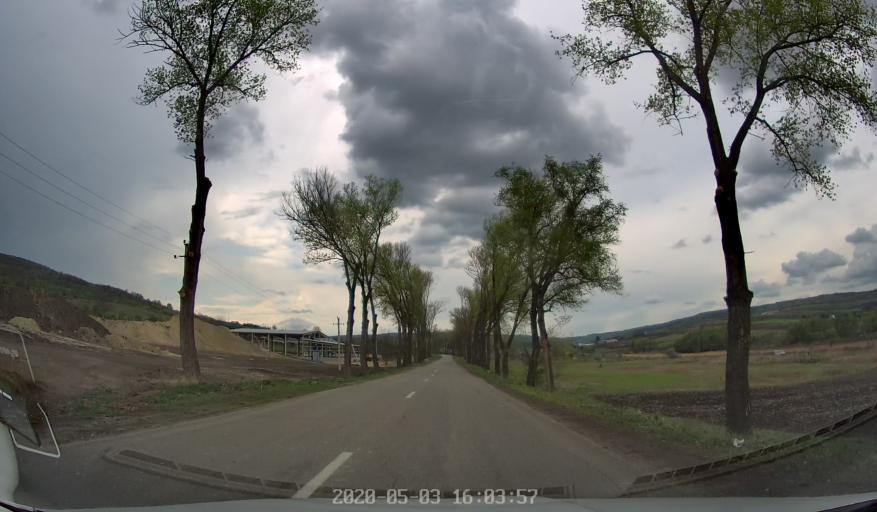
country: MD
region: Stinga Nistrului
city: Bucovat
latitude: 47.1834
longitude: 28.3742
